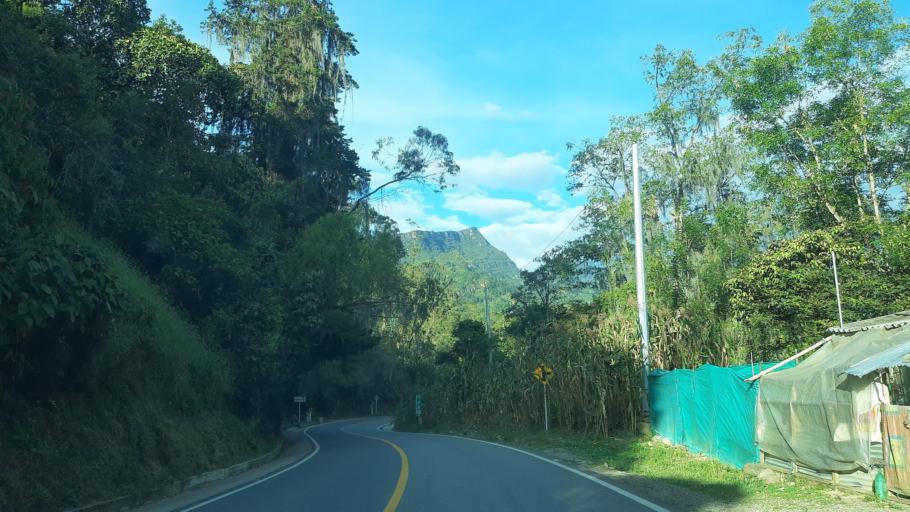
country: CO
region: Cundinamarca
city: Macheta
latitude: 5.0756
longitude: -73.5636
